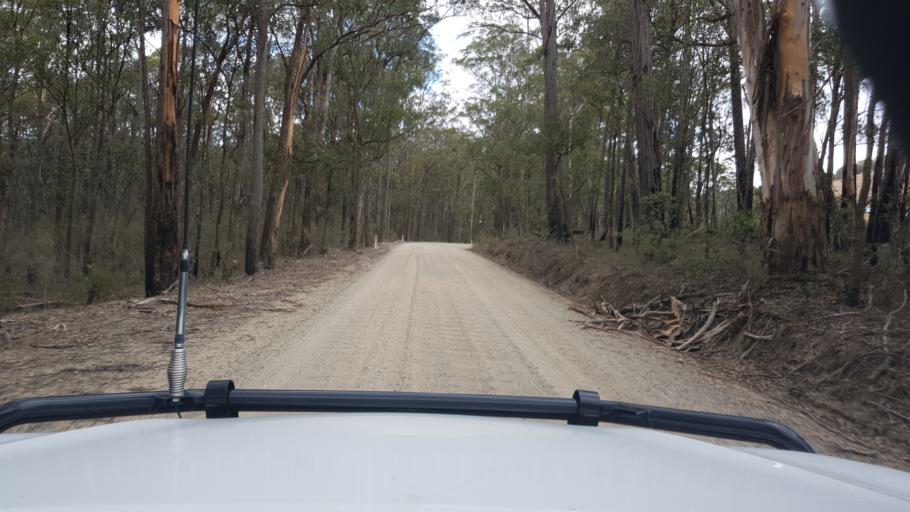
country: AU
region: Victoria
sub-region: East Gippsland
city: Bairnsdale
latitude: -37.6869
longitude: 147.5607
